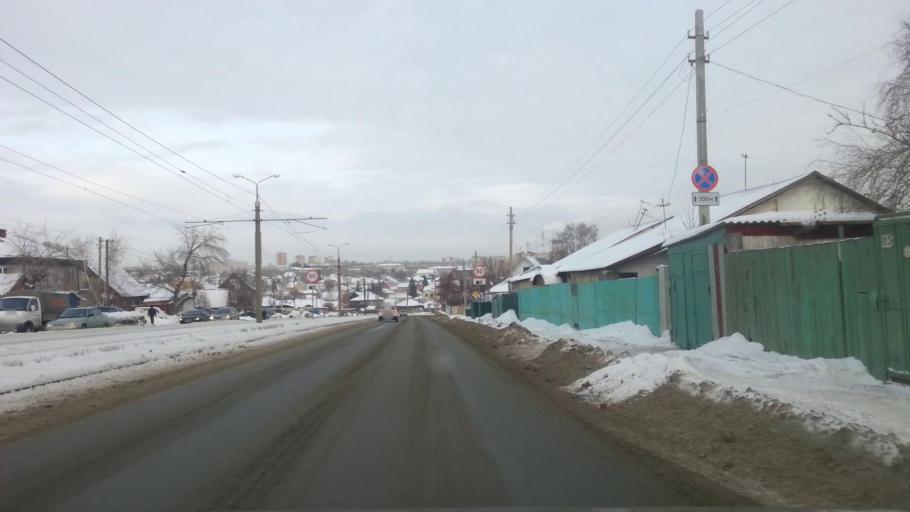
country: RU
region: Altai Krai
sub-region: Gorod Barnaulskiy
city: Barnaul
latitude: 53.3645
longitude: 83.7302
